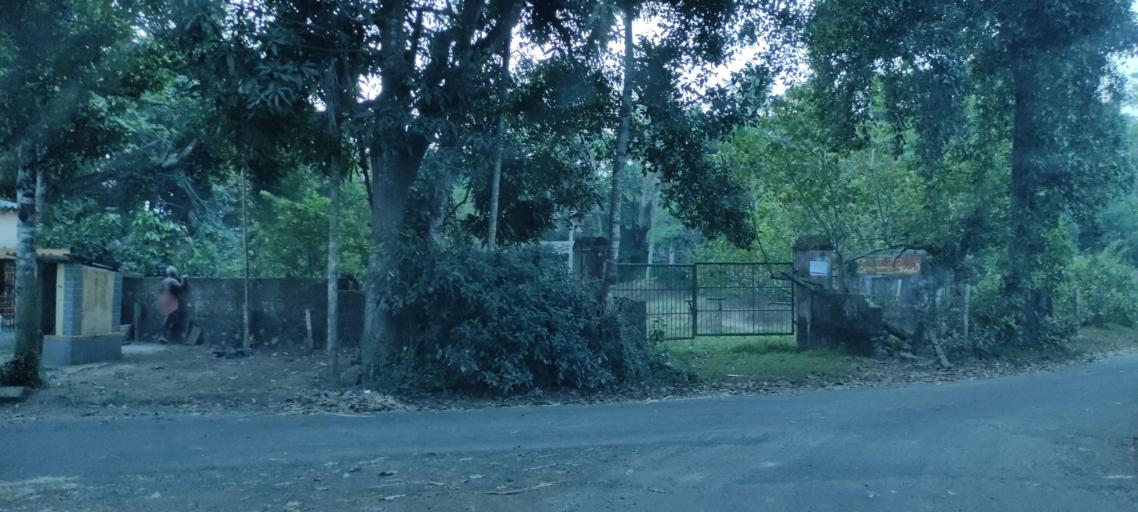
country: IN
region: Kerala
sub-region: Alappuzha
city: Mavelikara
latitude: 9.3307
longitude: 76.4901
